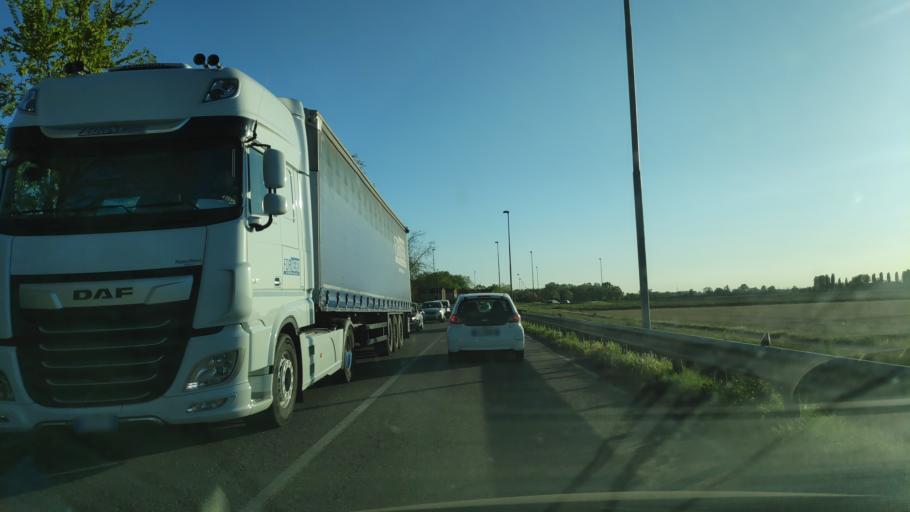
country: IT
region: Lombardy
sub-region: Citta metropolitana di Milano
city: Pieve Emanuele
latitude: 45.3506
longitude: 9.1964
